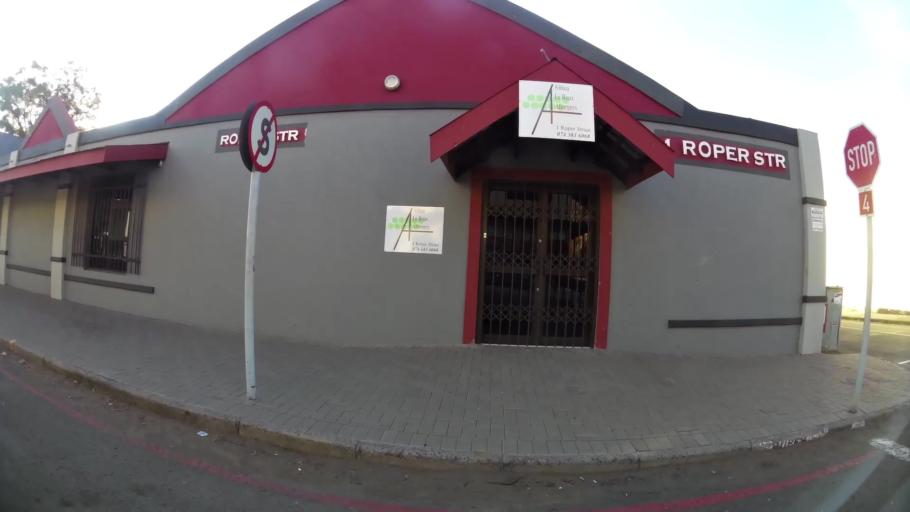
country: ZA
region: Northern Cape
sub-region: Frances Baard District Municipality
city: Kimberley
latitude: -28.7358
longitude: 24.7648
